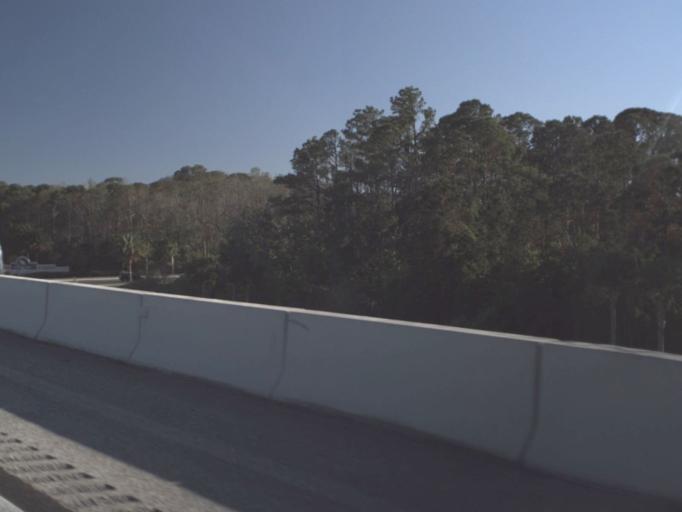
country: US
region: Florida
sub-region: Flagler County
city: Flagler Beach
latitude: 29.4776
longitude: -81.1846
